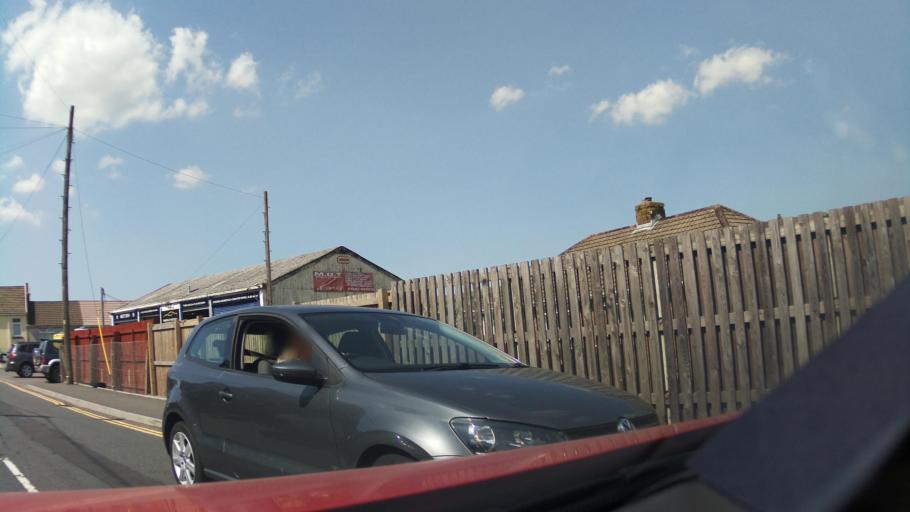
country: GB
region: Wales
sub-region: Caerphilly County Borough
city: Rhymney
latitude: 51.7415
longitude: -3.2763
